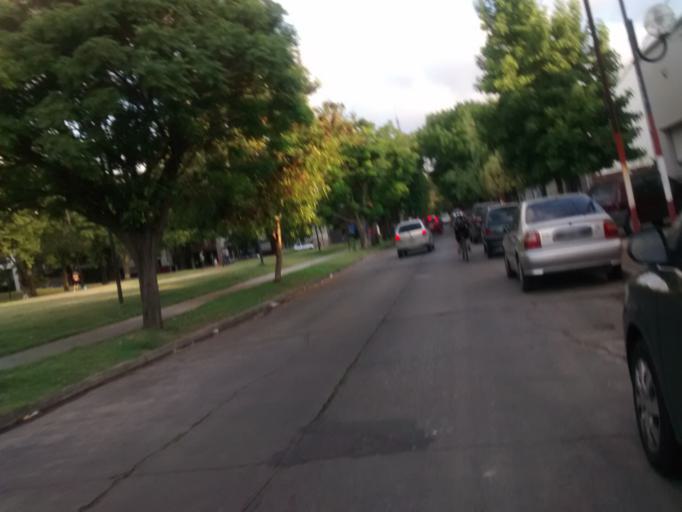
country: AR
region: Buenos Aires
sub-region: Partido de La Plata
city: La Plata
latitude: -34.9133
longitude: -57.9679
